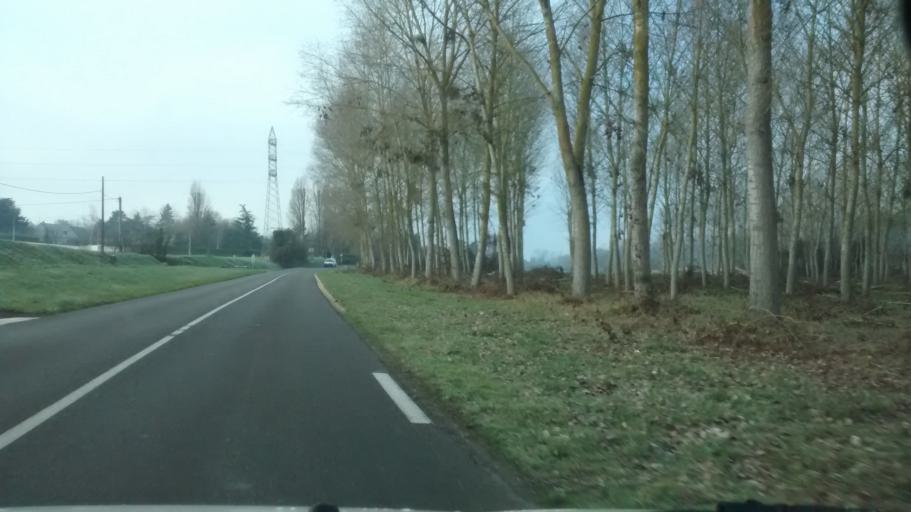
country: FR
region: Centre
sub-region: Departement d'Indre-et-Loire
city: Ballan-Mire
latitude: 47.3641
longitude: 0.6304
